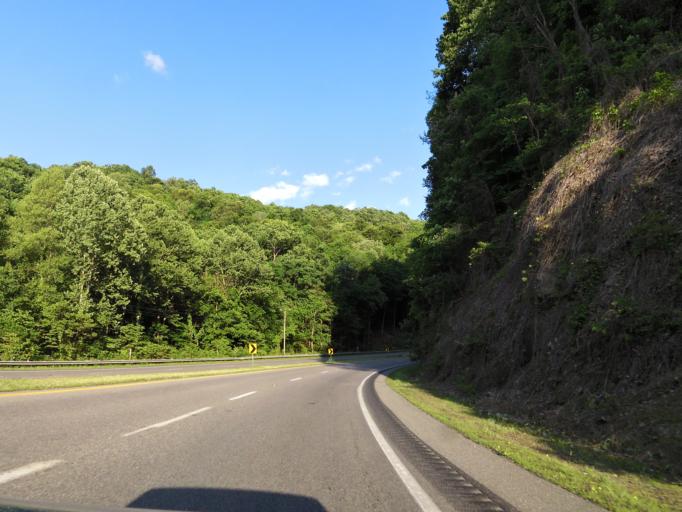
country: US
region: Virginia
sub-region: Washington County
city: Abingdon
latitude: 36.7692
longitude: -82.0695
